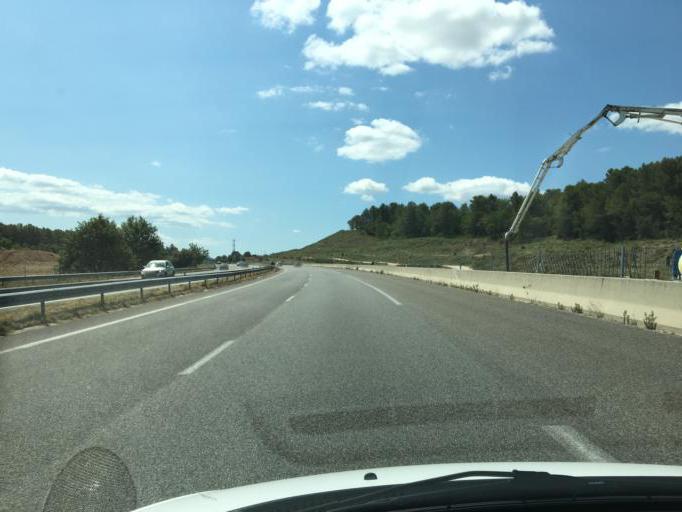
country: FR
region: Provence-Alpes-Cote d'Azur
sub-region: Departement des Bouches-du-Rhone
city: Belcodene
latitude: 43.4205
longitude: 5.5748
